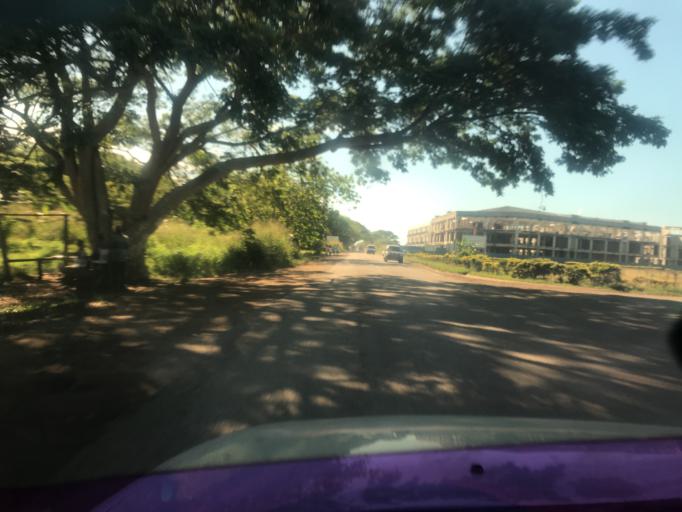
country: SB
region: Guadalcanal
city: Honiara
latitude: -9.4258
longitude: 160.0459
